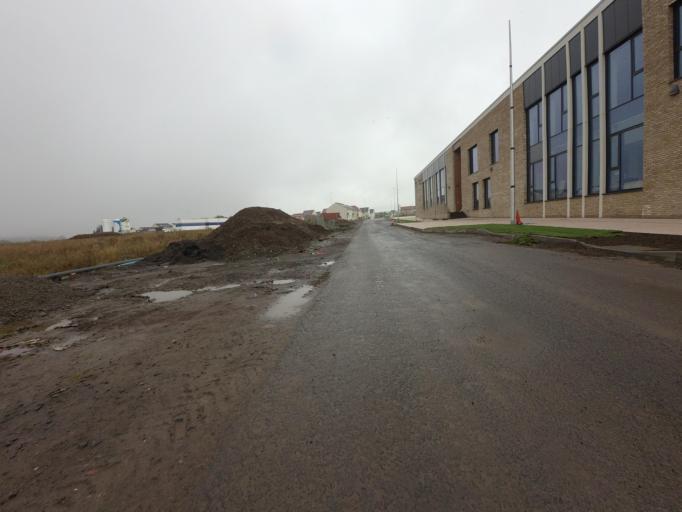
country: GB
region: Scotland
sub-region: West Lothian
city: East Calder
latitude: 55.9051
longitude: -3.4472
